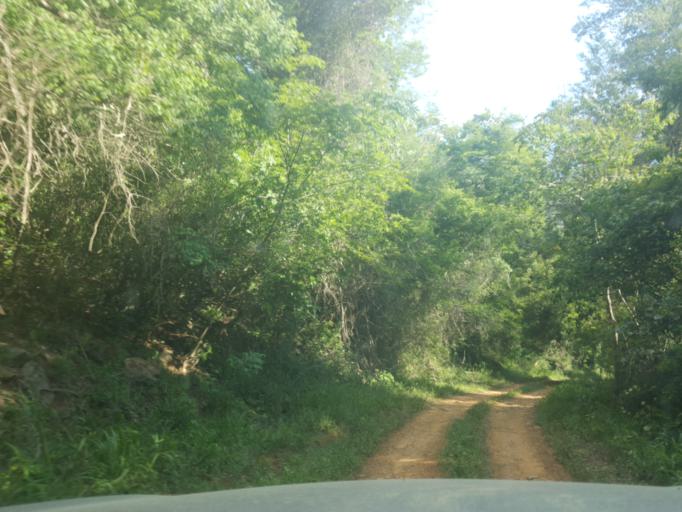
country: ZA
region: Limpopo
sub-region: Mopani District Municipality
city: Hoedspruit
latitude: -24.5895
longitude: 30.8435
